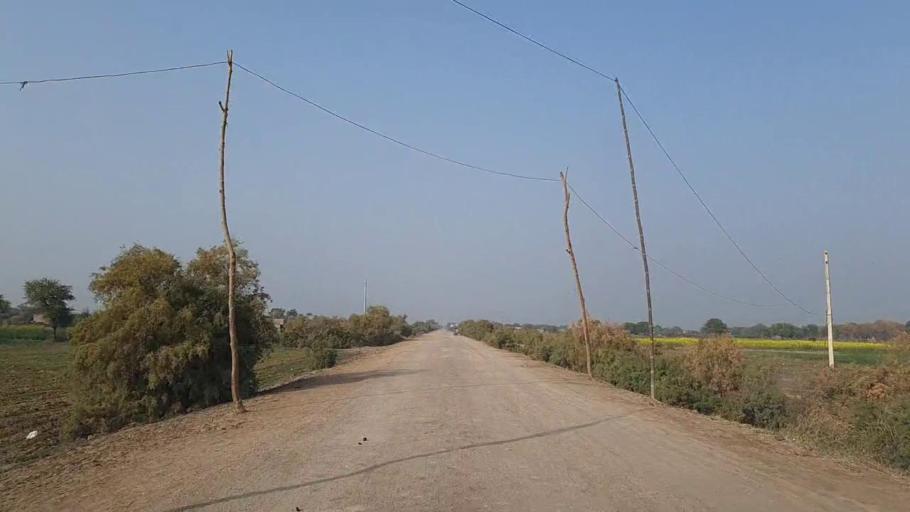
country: PK
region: Sindh
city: Nawabshah
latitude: 26.3335
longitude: 68.4891
